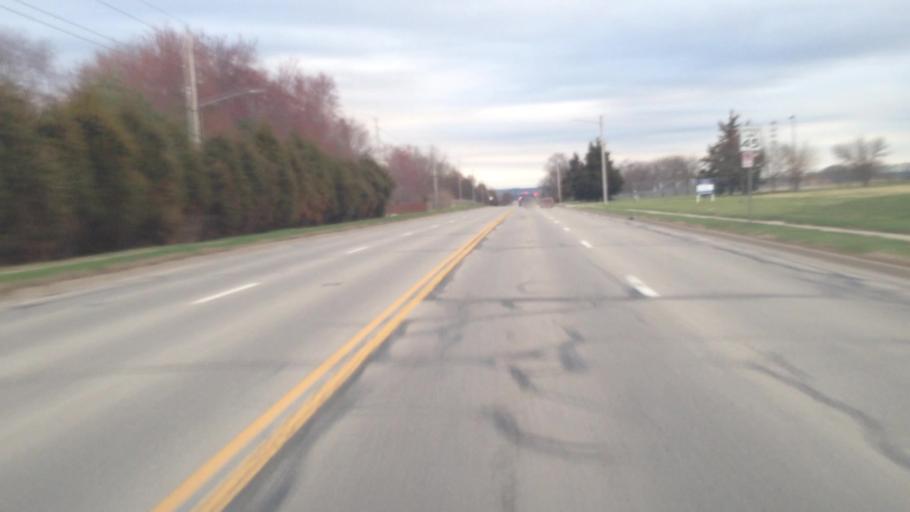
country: US
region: Kansas
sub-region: Douglas County
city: Lawrence
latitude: 38.9510
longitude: -95.3071
